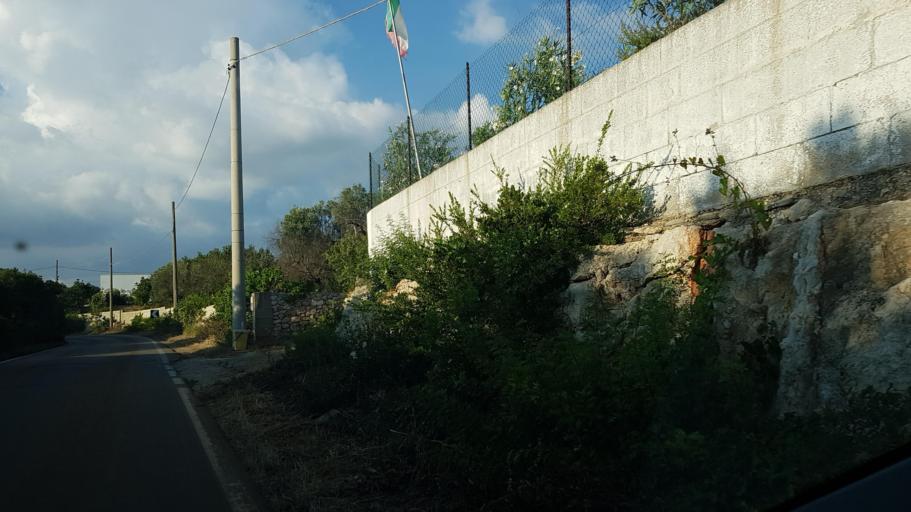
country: IT
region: Apulia
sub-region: Provincia di Lecce
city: Gemini
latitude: 39.8495
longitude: 18.2087
